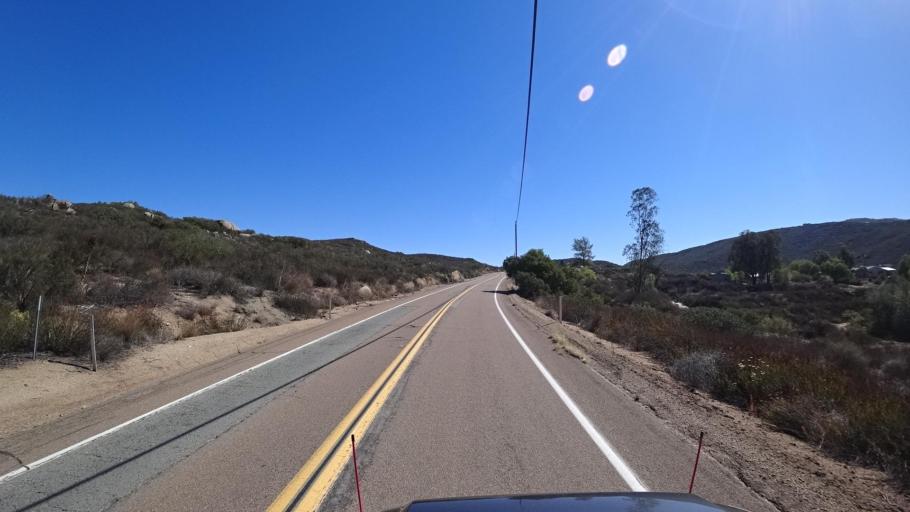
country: US
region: California
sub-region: San Diego County
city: Alpine
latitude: 32.7889
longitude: -116.7304
